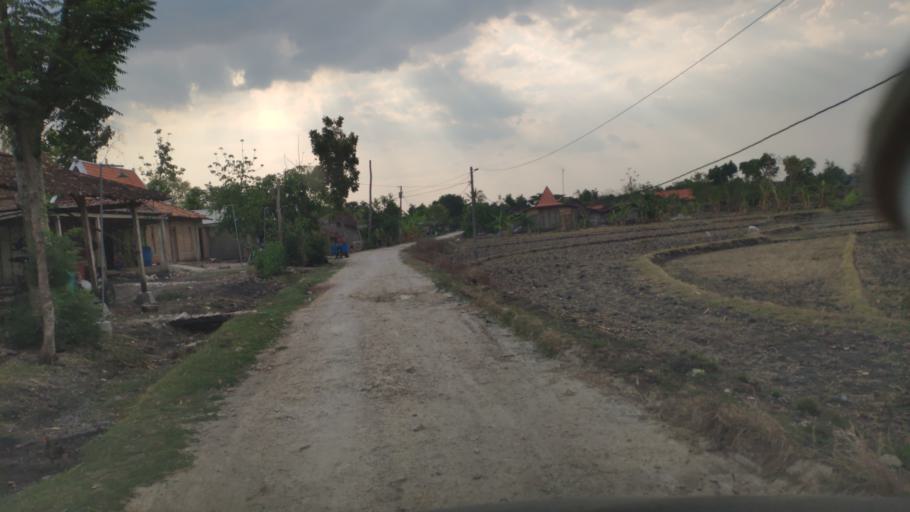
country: ID
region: Central Java
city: Randublatung
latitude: -7.2857
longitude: 111.2681
